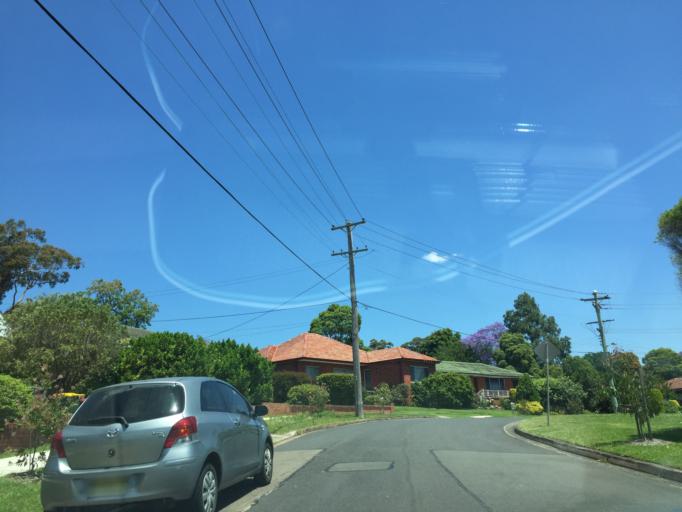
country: AU
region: New South Wales
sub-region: Parramatta
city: Dundas Valley
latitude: -33.7895
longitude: 151.0659
